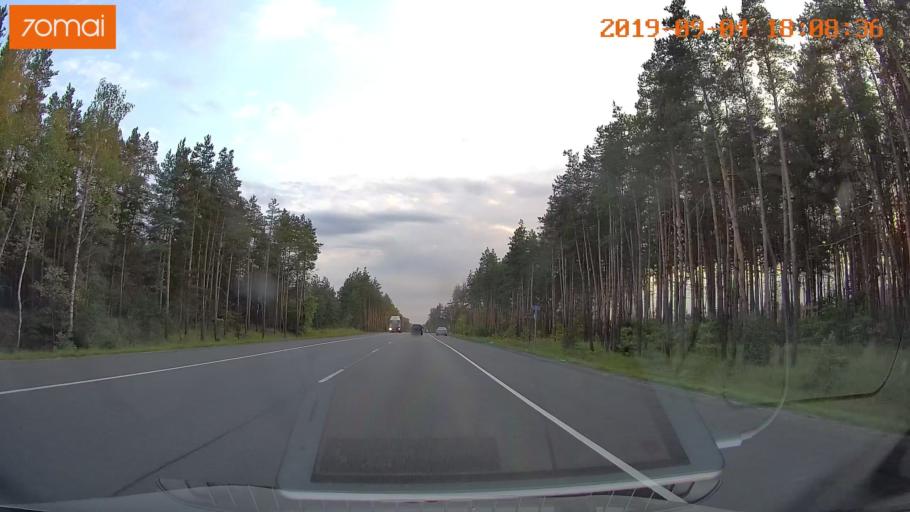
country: RU
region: Moskovskaya
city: Khorlovo
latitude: 55.4040
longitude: 38.7837
